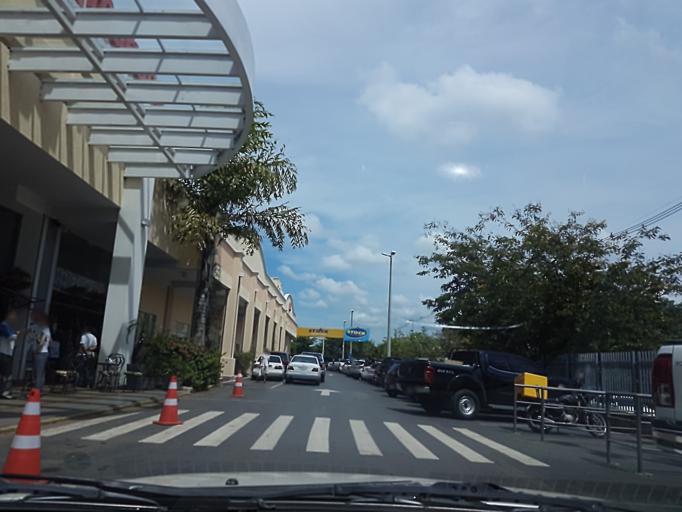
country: PY
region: Central
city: Colonia Mariano Roque Alonso
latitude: -25.2254
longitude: -57.5365
